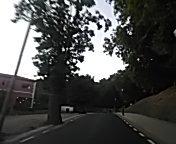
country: ES
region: Castille and Leon
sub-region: Provincia de Salamanca
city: Bejar
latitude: 40.3791
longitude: -5.7633
